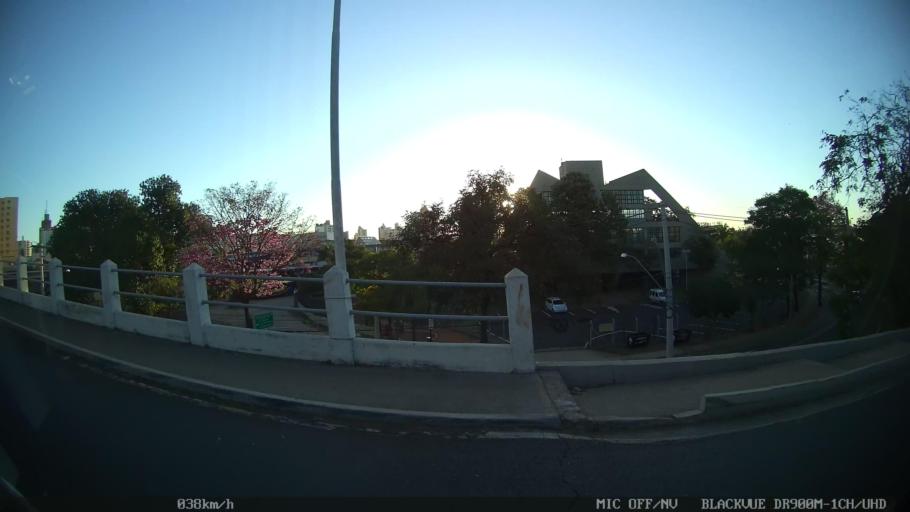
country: BR
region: Sao Paulo
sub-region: Sao Jose Do Rio Preto
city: Sao Jose do Rio Preto
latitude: -20.8094
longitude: -49.3748
